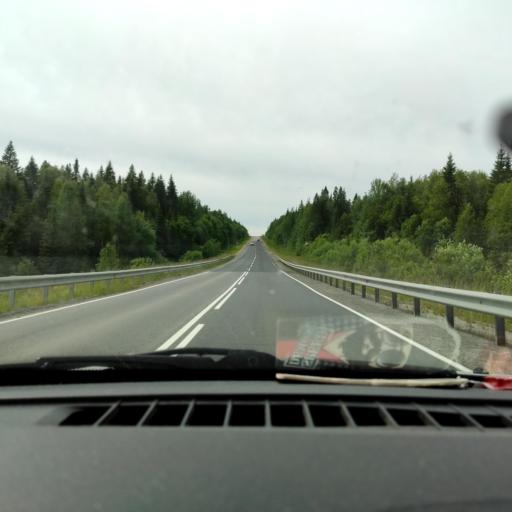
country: RU
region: Perm
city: Chusovoy
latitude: 58.3737
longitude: 57.9784
